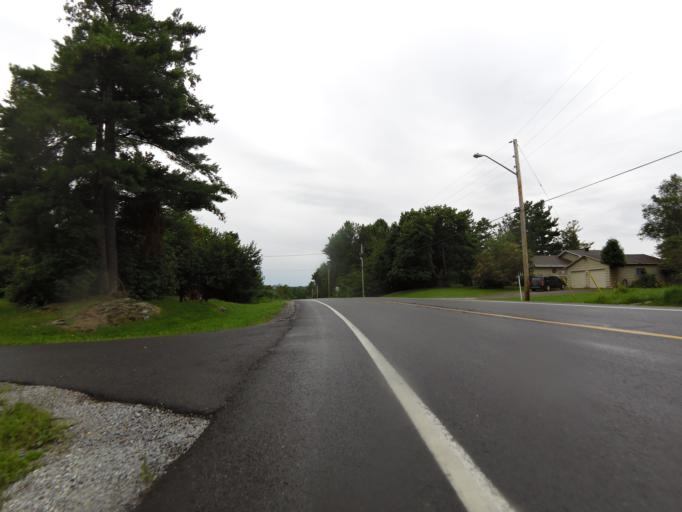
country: CA
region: Ontario
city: Perth
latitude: 45.0126
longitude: -76.3681
